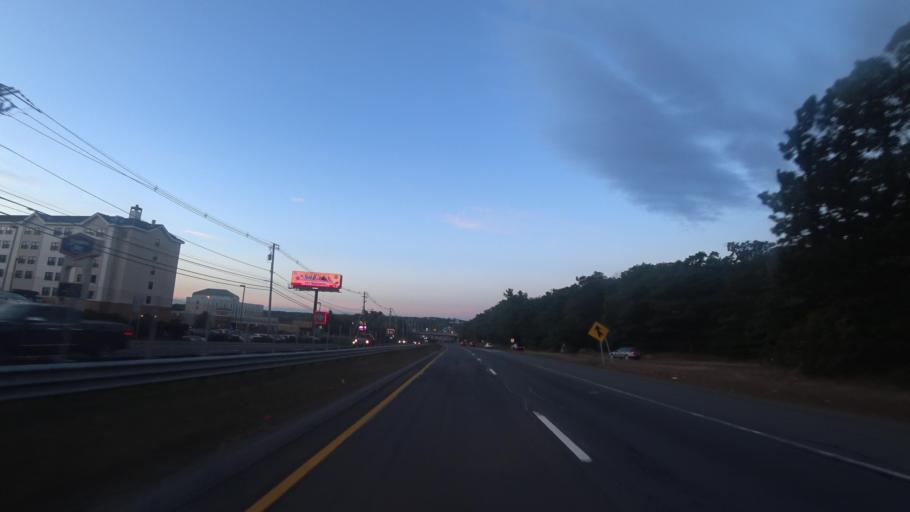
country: US
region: Massachusetts
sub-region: Essex County
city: South Peabody
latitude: 42.5272
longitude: -70.9945
